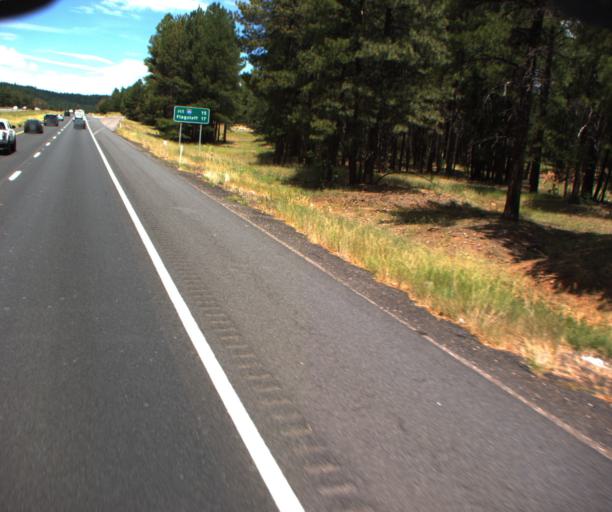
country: US
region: Arizona
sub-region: Coconino County
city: Sedona
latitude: 34.9502
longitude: -111.6659
